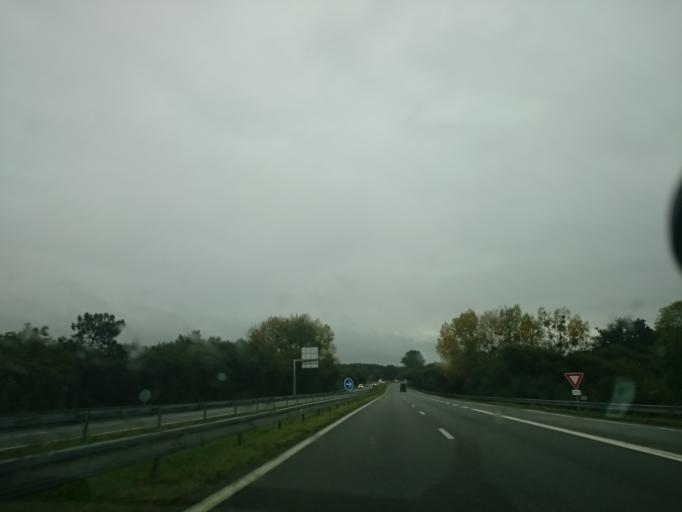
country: FR
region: Brittany
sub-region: Departement du Morbihan
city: Theix
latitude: 47.6316
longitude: -2.6470
